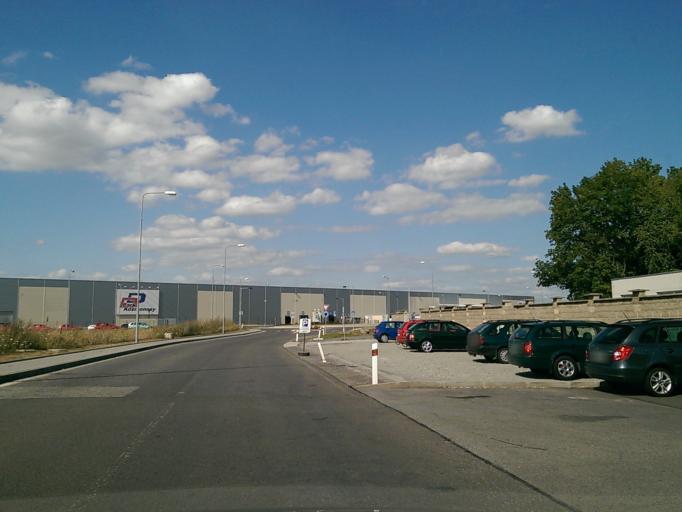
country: CZ
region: Central Bohemia
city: Kosmonosy
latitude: 50.4285
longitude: 14.9394
